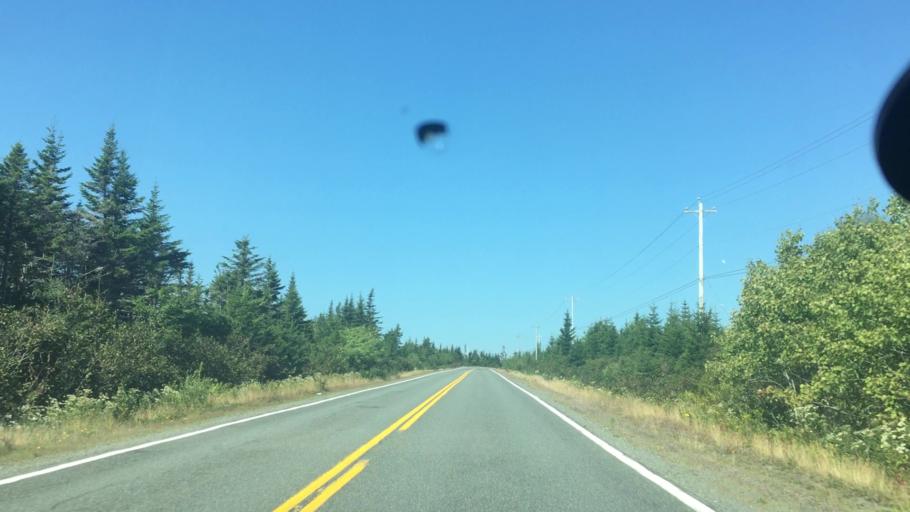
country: CA
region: Nova Scotia
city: Antigonish
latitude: 44.9823
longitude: -62.0934
